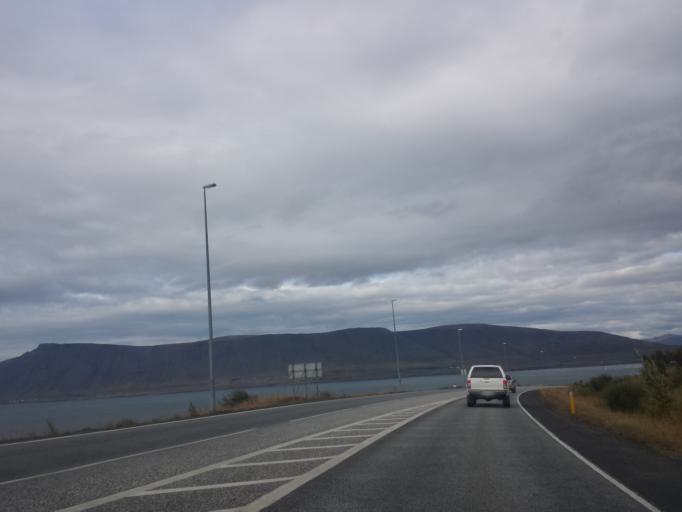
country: IS
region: Capital Region
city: Reykjavik
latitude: 64.2761
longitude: -21.8402
